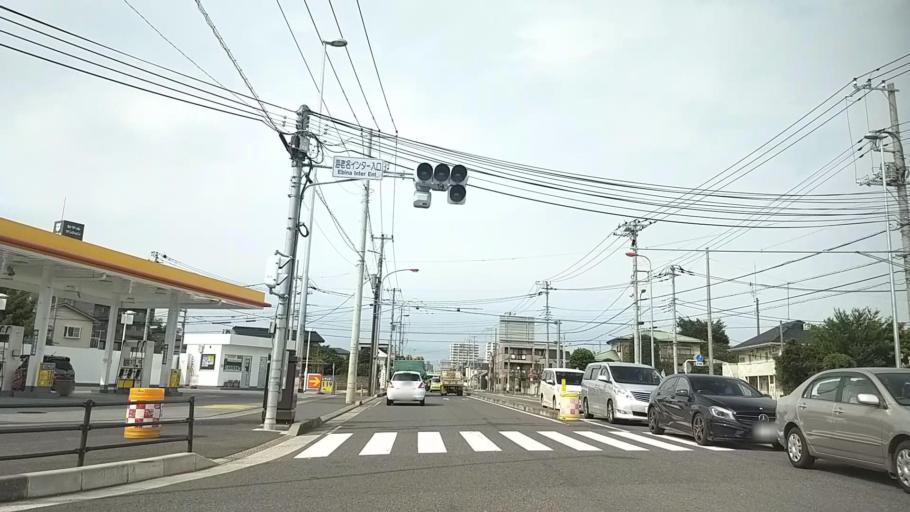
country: JP
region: Kanagawa
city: Atsugi
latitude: 35.4359
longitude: 139.3833
